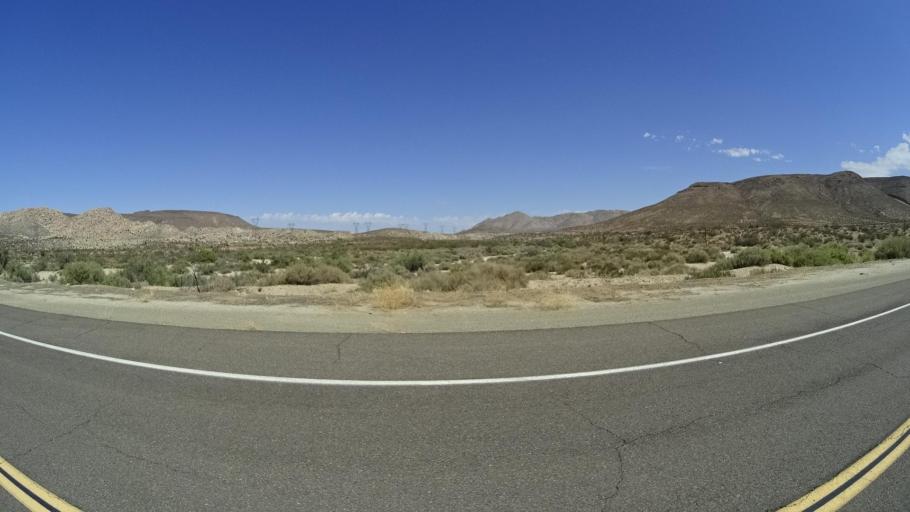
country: MX
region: Baja California
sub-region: Tecate
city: Cereso del Hongo
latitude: 32.6247
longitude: -116.1598
